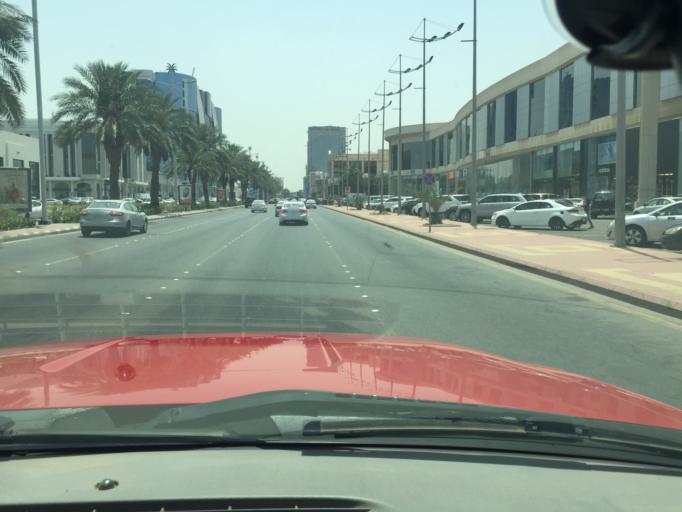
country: SA
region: Makkah
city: Jeddah
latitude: 21.5530
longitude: 39.1642
